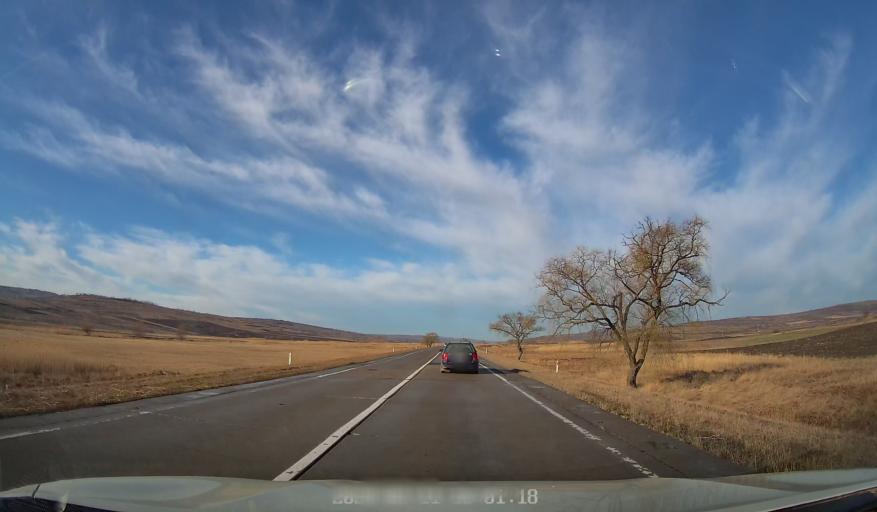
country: MD
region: Taraclia
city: Telenesti
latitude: 47.3887
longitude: 28.4177
